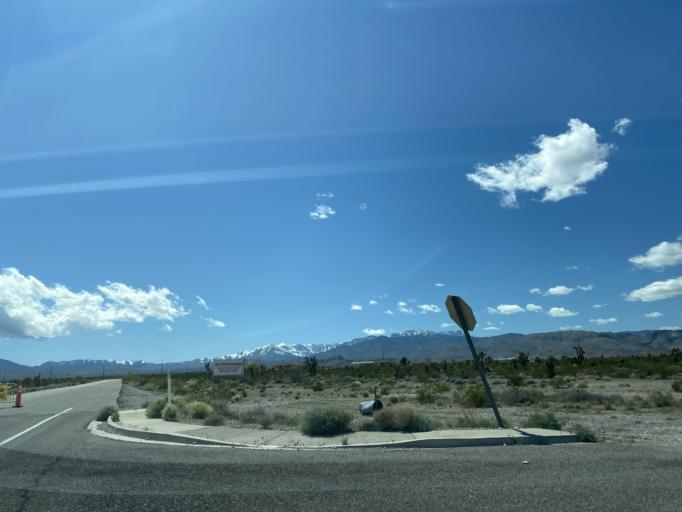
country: US
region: Nevada
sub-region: Clark County
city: Summerlin South
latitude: 36.3592
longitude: -115.3552
